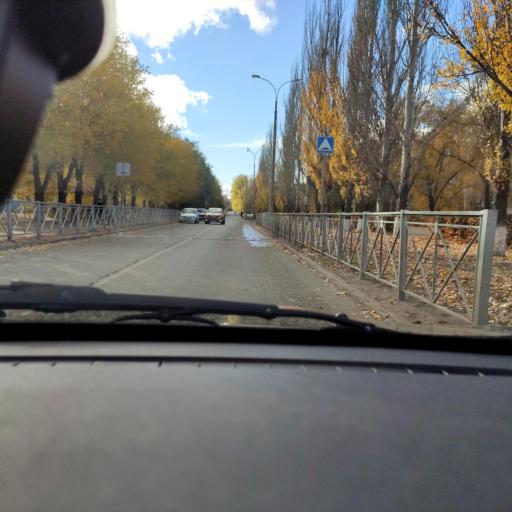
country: RU
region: Samara
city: Tol'yatti
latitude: 53.5304
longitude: 49.2922
